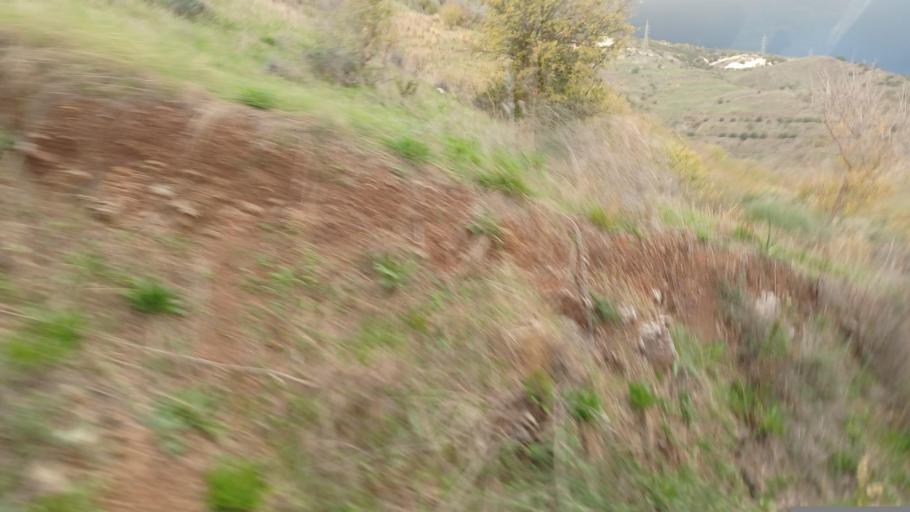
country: CY
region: Pafos
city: Mesogi
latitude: 34.7864
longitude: 32.5213
